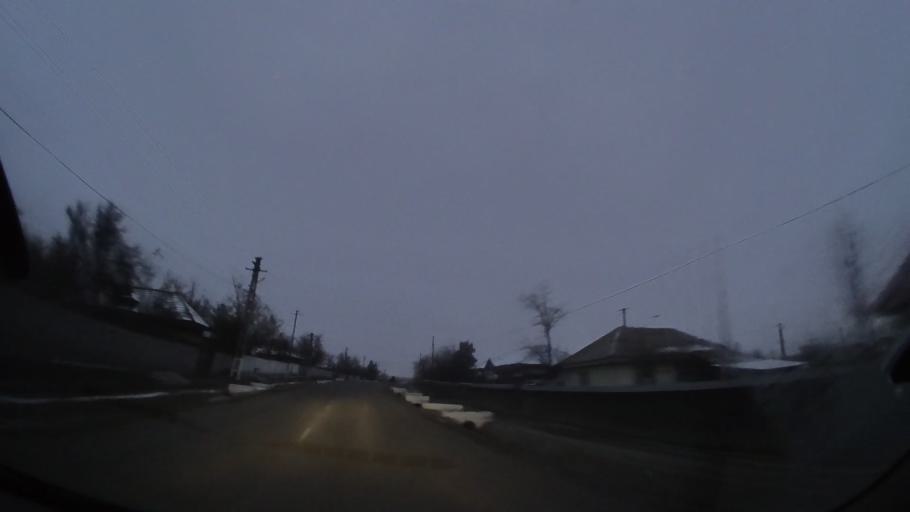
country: RO
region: Vaslui
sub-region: Comuna Dimitrie Cantemir
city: Dimitrie Cantemir
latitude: 46.4601
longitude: 28.0275
